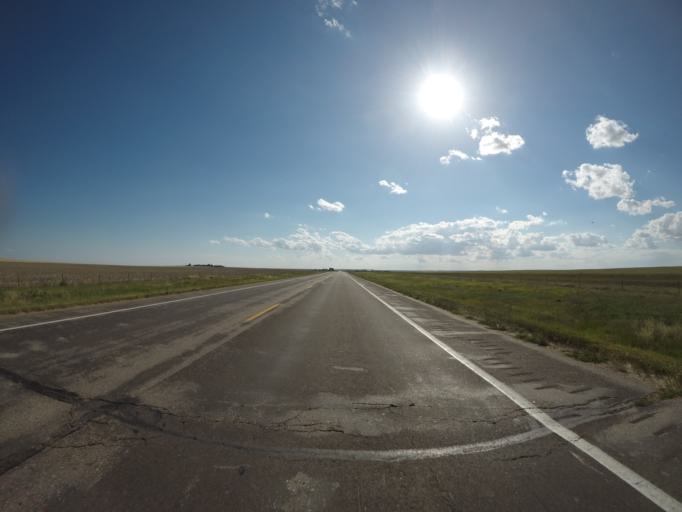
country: US
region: Colorado
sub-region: Morgan County
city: Fort Morgan
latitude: 40.6019
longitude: -103.8610
